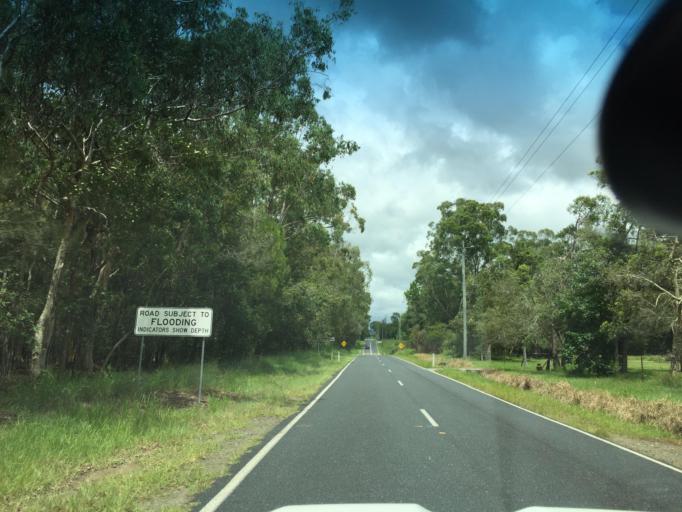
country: AU
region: Queensland
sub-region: Moreton Bay
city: Caboolture
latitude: -27.0487
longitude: 152.9121
